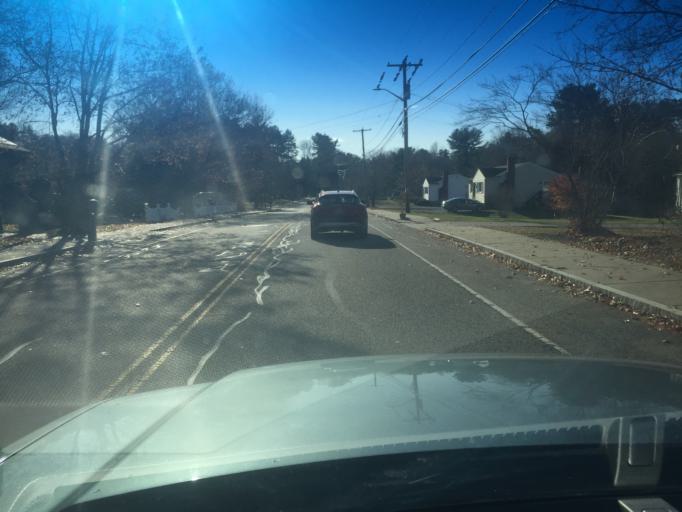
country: US
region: Massachusetts
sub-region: Norfolk County
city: Medway
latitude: 42.1126
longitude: -71.4296
